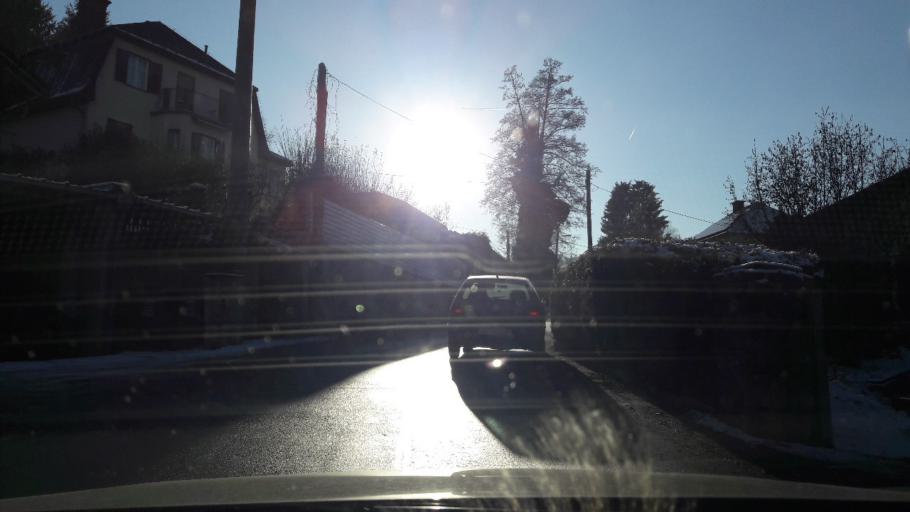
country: AT
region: Styria
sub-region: Graz Stadt
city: Mariatrost
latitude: 47.0991
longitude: 15.4787
